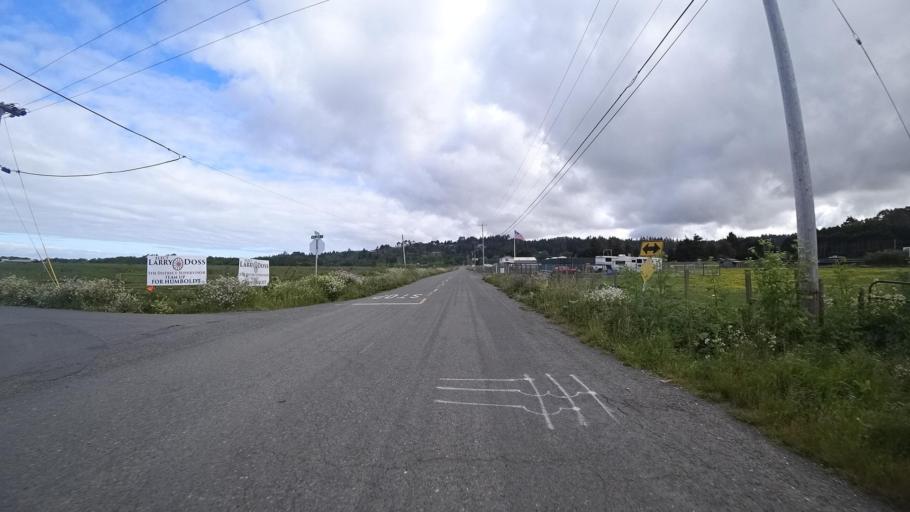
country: US
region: California
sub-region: Humboldt County
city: McKinleyville
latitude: 40.9086
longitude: -124.0914
